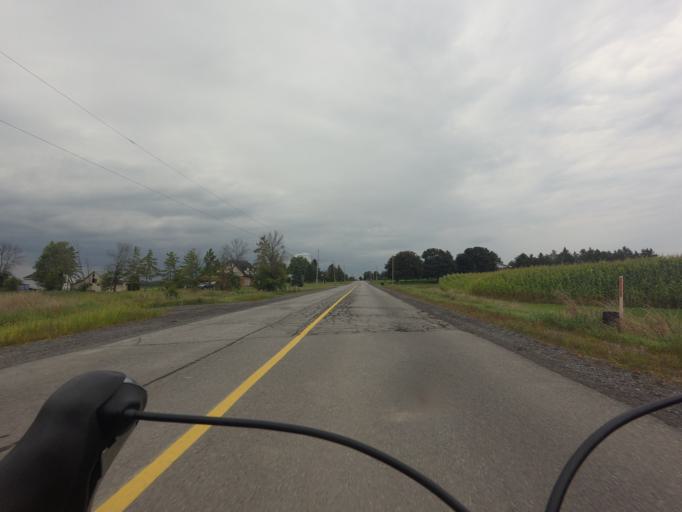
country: CA
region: Ontario
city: Bells Corners
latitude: 45.1361
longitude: -75.7786
